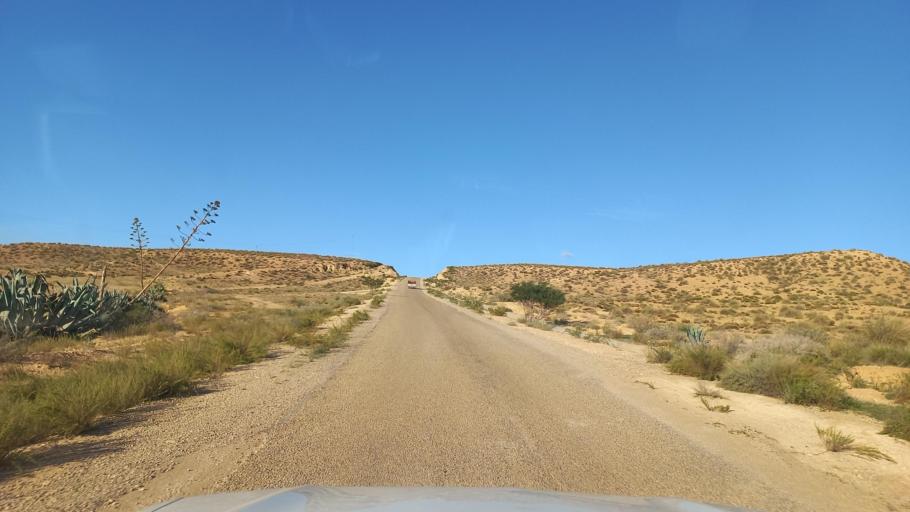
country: TN
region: Al Qasrayn
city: Sbiba
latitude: 35.3470
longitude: 9.1301
